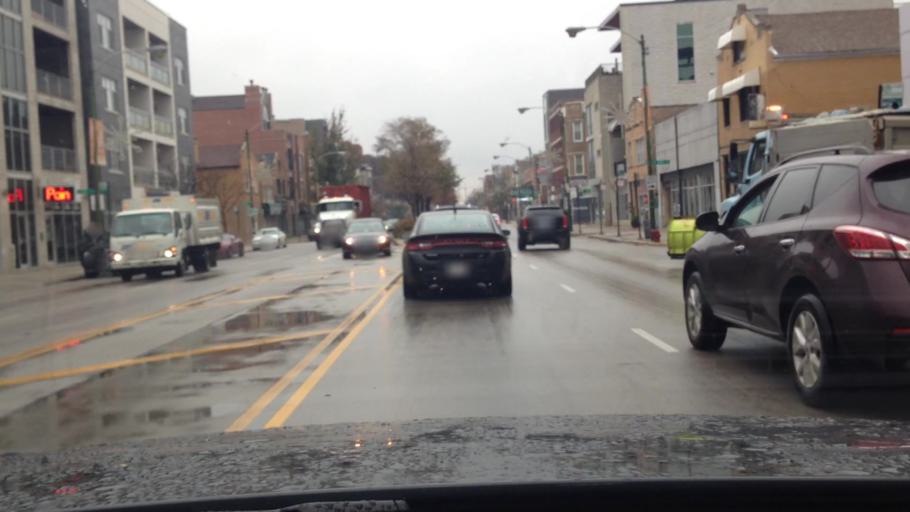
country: US
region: Illinois
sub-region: Cook County
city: Chicago
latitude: 41.8967
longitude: -87.6673
